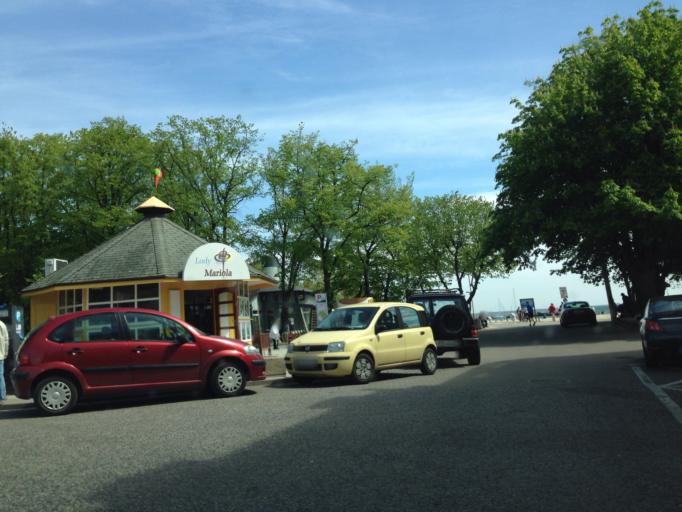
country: PL
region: Pomeranian Voivodeship
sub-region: Gdynia
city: Gdynia
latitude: 54.5162
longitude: 18.5478
